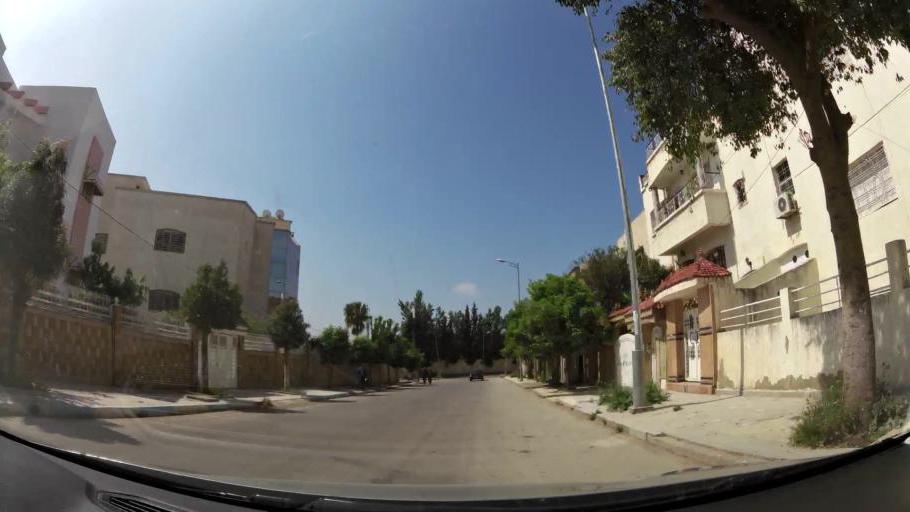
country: MA
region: Fes-Boulemane
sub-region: Fes
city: Fes
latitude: 34.0534
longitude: -5.0337
